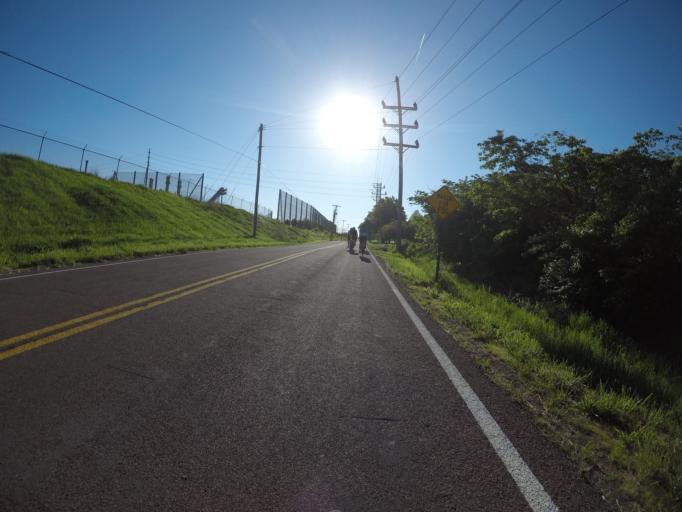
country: US
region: Kansas
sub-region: Shawnee County
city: Topeka
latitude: 39.0515
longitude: -95.5718
